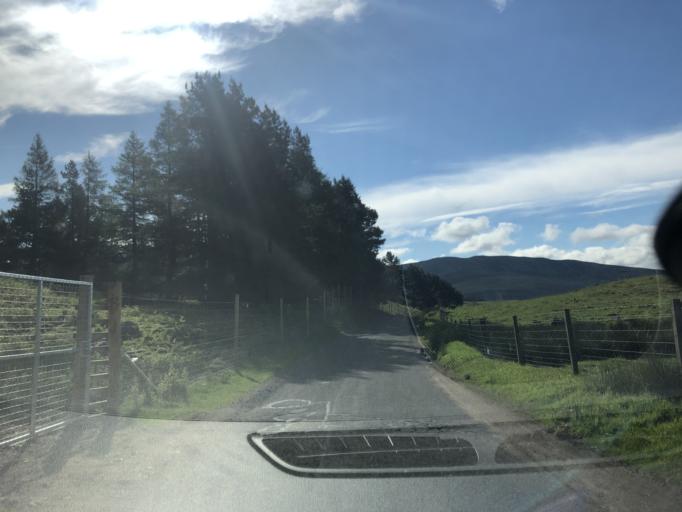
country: GB
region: Scotland
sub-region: Angus
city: Kirriemuir
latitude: 56.8295
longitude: -3.0590
